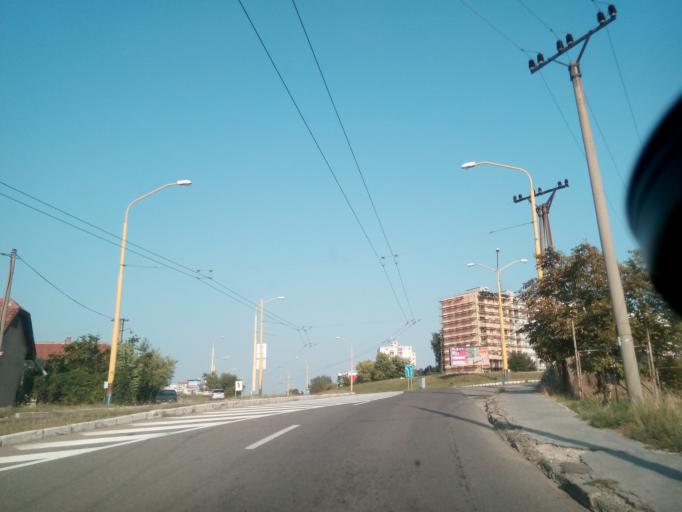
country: SK
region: Kosicky
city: Kosice
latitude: 48.7107
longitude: 21.2080
